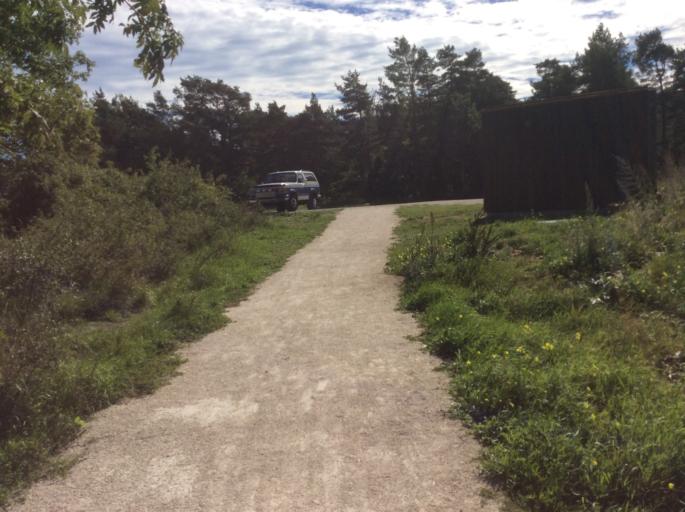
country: SE
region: Gotland
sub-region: Gotland
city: Vibble
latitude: 57.6182
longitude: 18.2684
